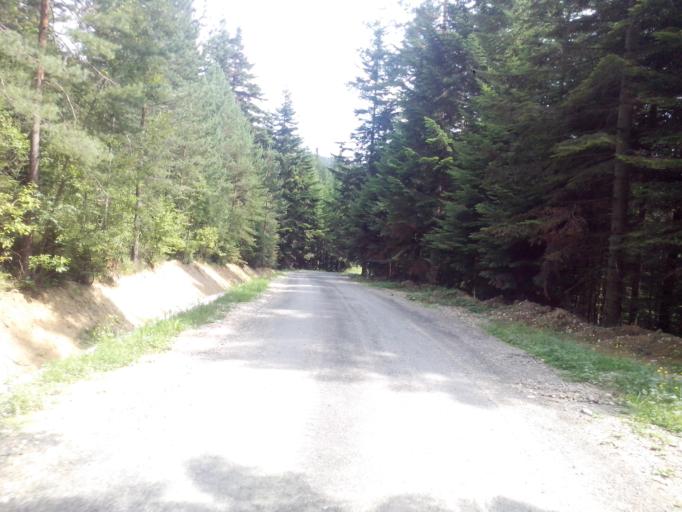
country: PL
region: Subcarpathian Voivodeship
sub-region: Powiat strzyzowski
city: Strzyzow
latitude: 49.8087
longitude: 21.8054
